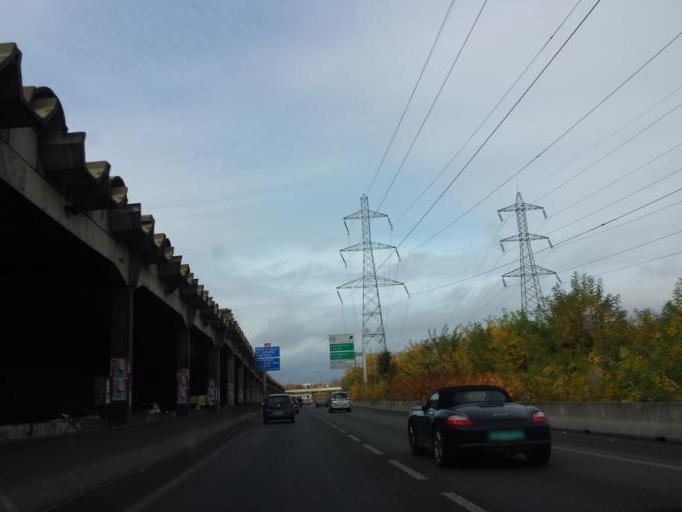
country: FR
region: Ile-de-France
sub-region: Departement des Hauts-de-Seine
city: Bois-Colombes
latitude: 48.9344
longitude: 2.2706
